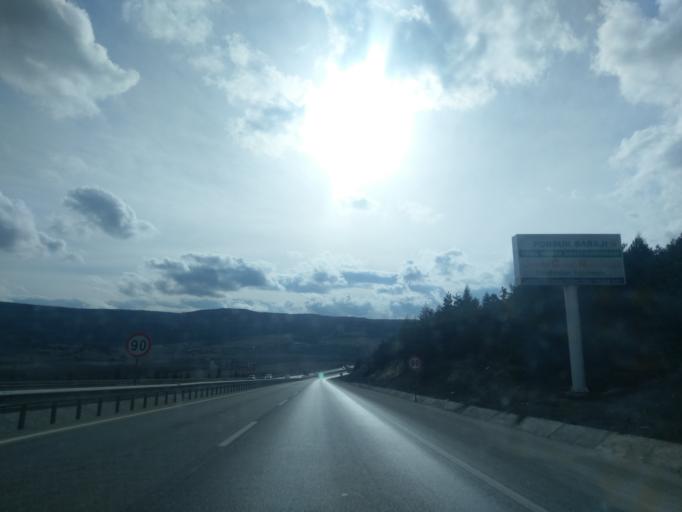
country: TR
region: Kuetahya
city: Sabuncu
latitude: 39.5760
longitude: 30.1189
